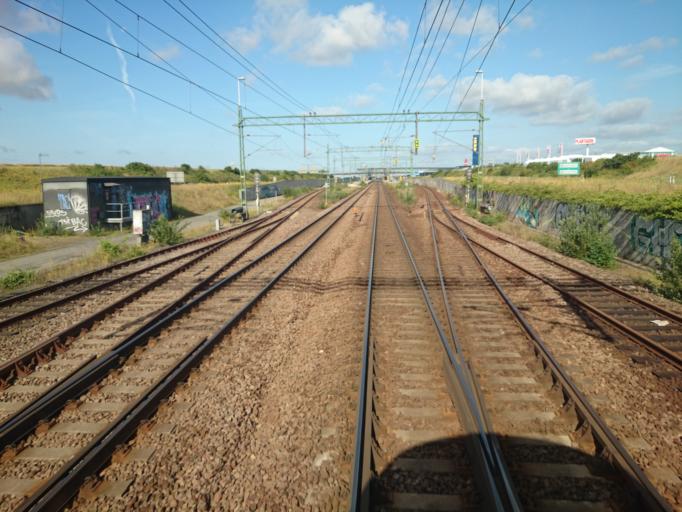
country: SE
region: Skane
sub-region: Malmo
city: Tygelsjo
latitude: 55.5475
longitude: 13.0000
